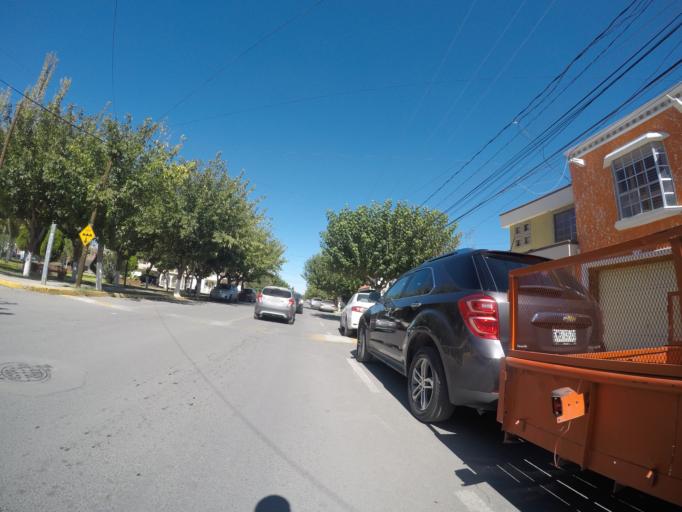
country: MX
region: Chihuahua
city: Ciudad Juarez
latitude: 31.7157
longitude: -106.4198
